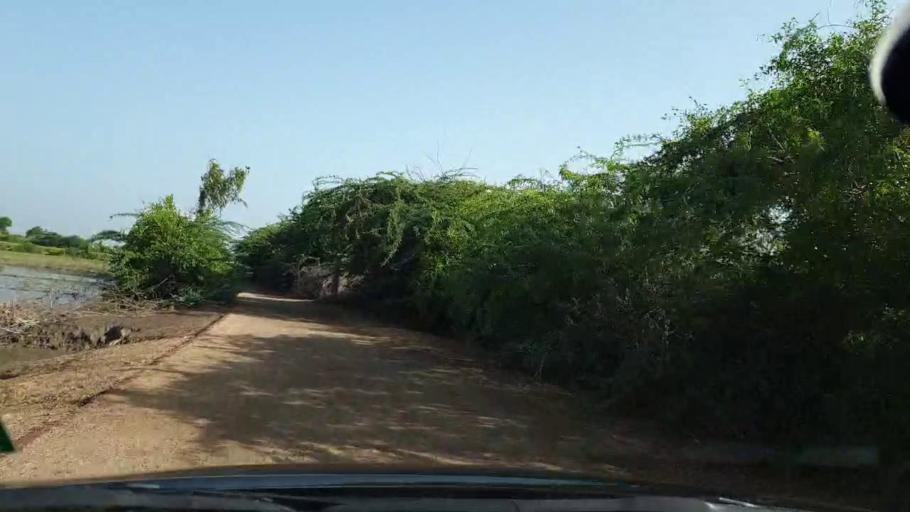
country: PK
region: Sindh
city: Tando Bago
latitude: 24.6585
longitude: 69.0421
